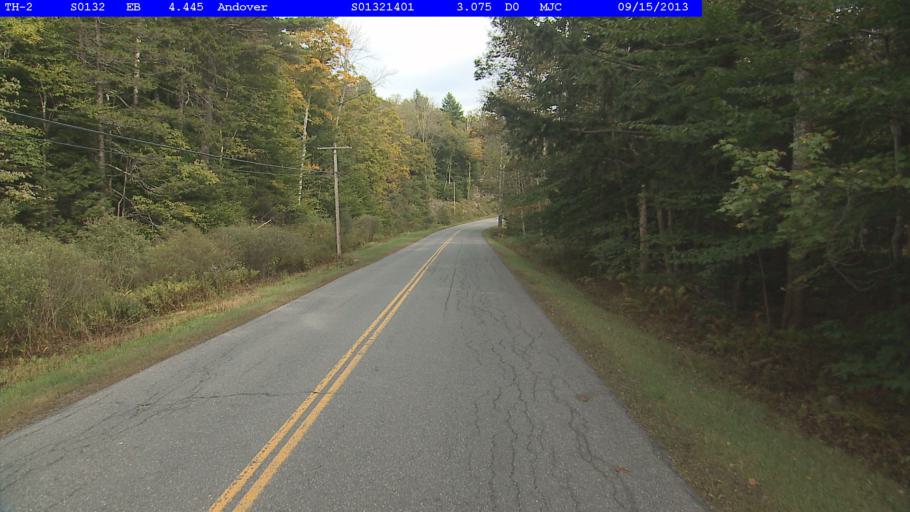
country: US
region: Vermont
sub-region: Windsor County
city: Chester
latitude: 43.2839
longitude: -72.7113
